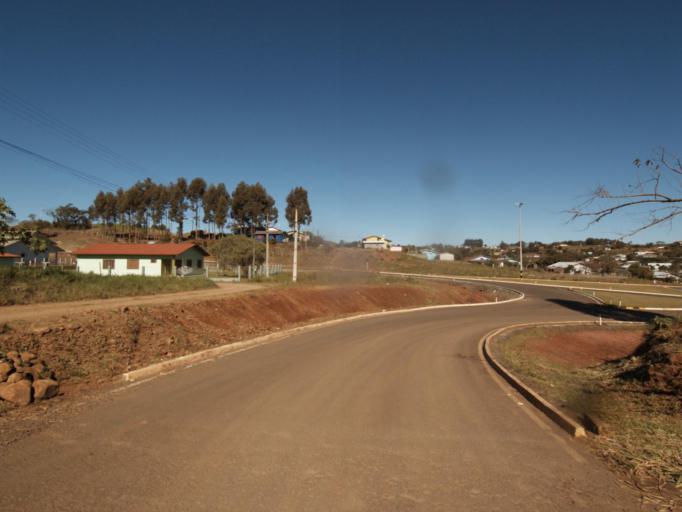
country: AR
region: Misiones
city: Bernardo de Irigoyen
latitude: -26.6134
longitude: -53.6732
